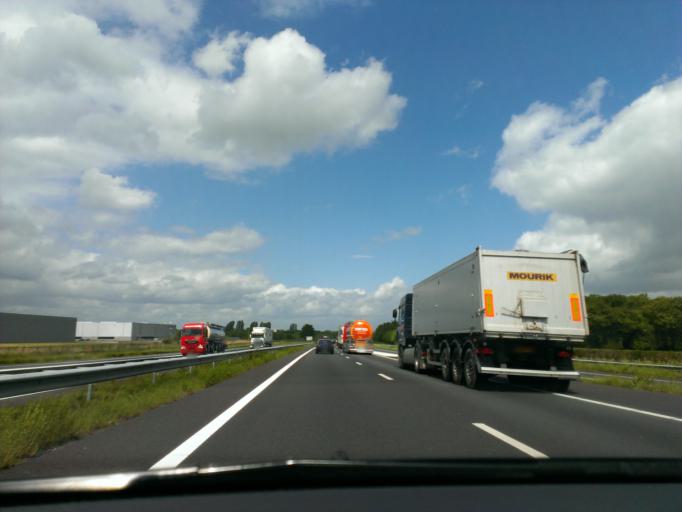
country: NL
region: Limburg
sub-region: Gemeente Venray
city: Venray
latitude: 51.4717
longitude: 6.0531
